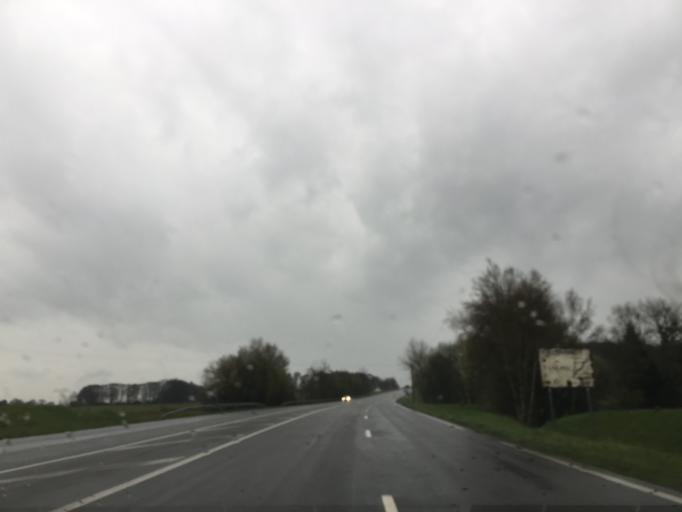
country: FR
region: Brittany
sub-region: Departement d'Ille-et-Vilaine
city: Luitre
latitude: 48.2829
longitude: -1.1520
